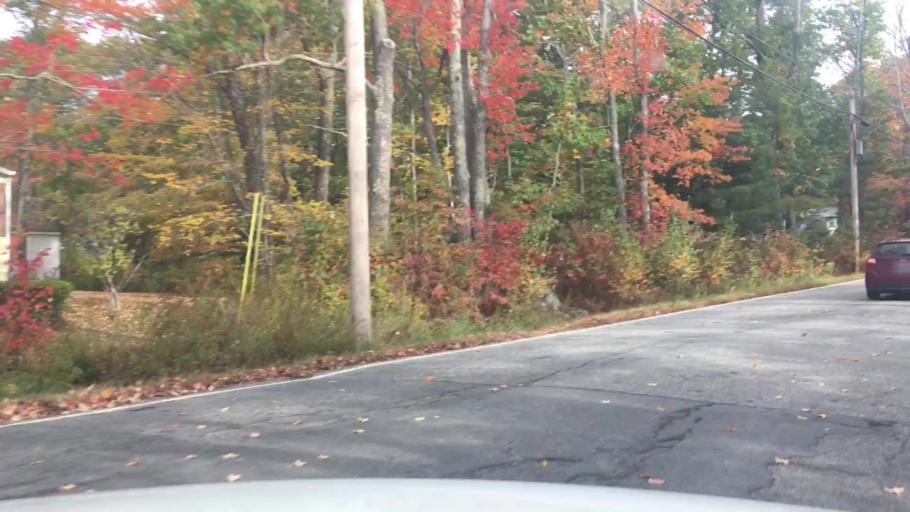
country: US
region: Maine
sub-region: Knox County
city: Rockport
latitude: 44.1738
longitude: -69.1221
